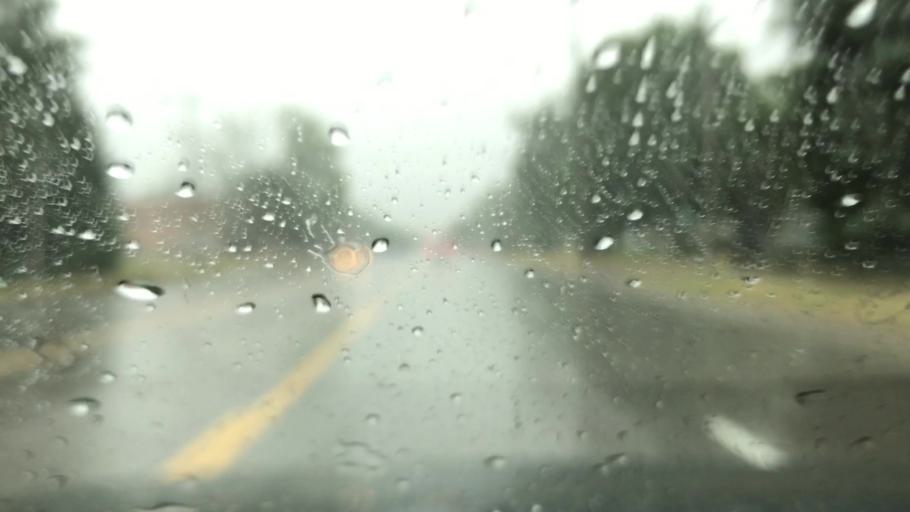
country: US
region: Michigan
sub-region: Kent County
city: Wyoming
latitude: 42.8868
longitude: -85.7243
